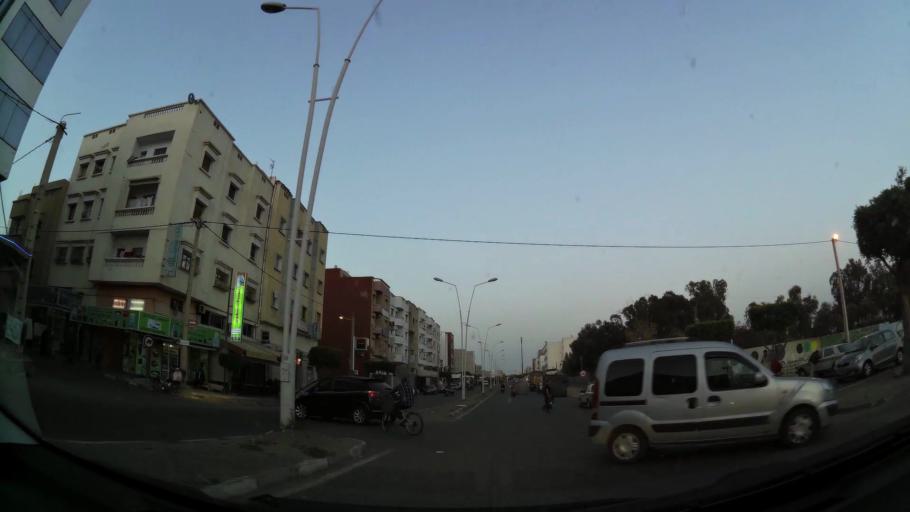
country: MA
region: Souss-Massa-Draa
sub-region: Inezgane-Ait Mellou
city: Inezgane
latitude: 30.3786
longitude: -9.5035
